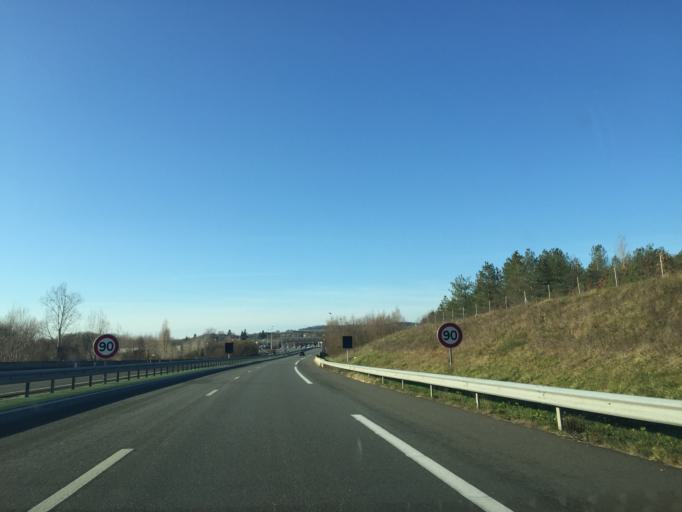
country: FR
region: Aquitaine
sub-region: Departement de la Dordogne
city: Montignac
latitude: 45.1488
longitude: 1.1742
